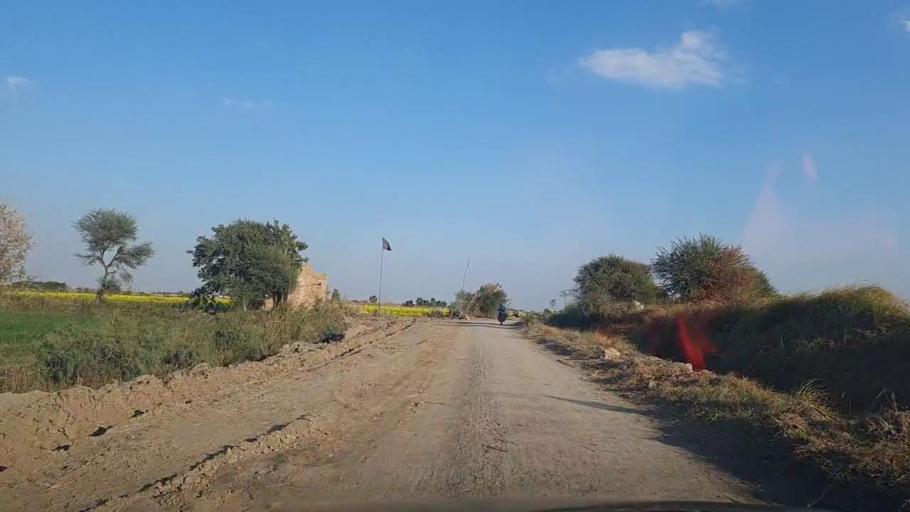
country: PK
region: Sindh
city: Jhol
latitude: 25.9209
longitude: 69.0374
